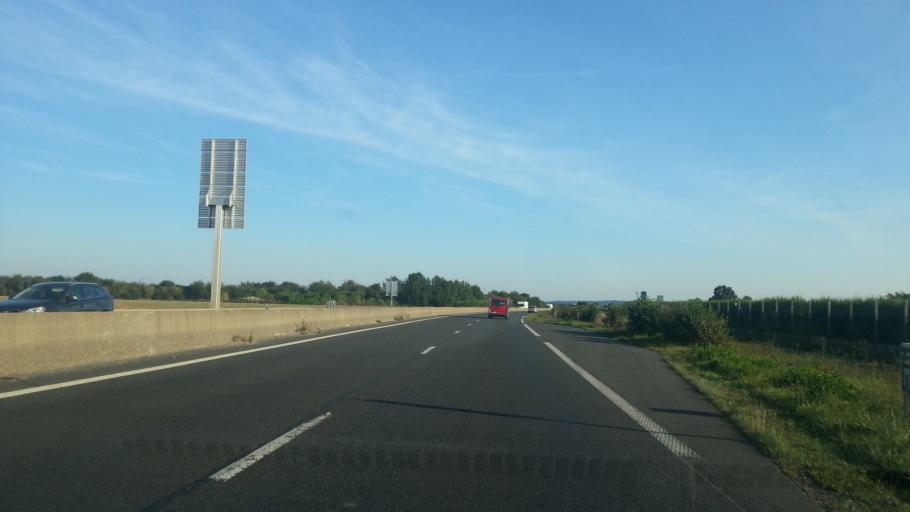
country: FR
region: Picardie
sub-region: Departement de l'Oise
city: Tille
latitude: 49.4448
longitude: 2.1091
